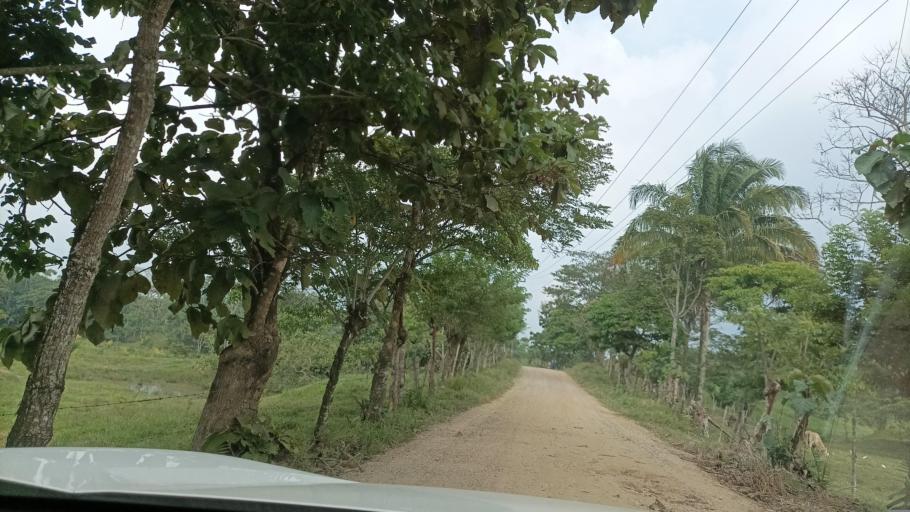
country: MX
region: Tabasco
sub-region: Huimanguillo
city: Francisco Rueda
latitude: 17.5890
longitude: -94.1999
